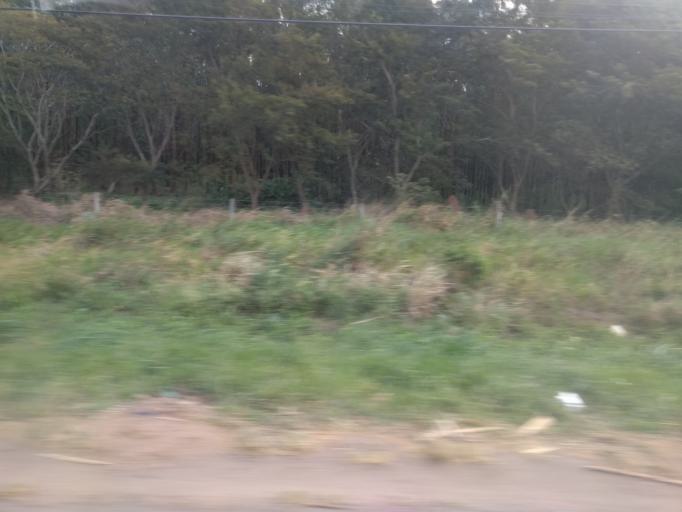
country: BO
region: Santa Cruz
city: La Belgica
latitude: -17.5653
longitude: -63.1590
